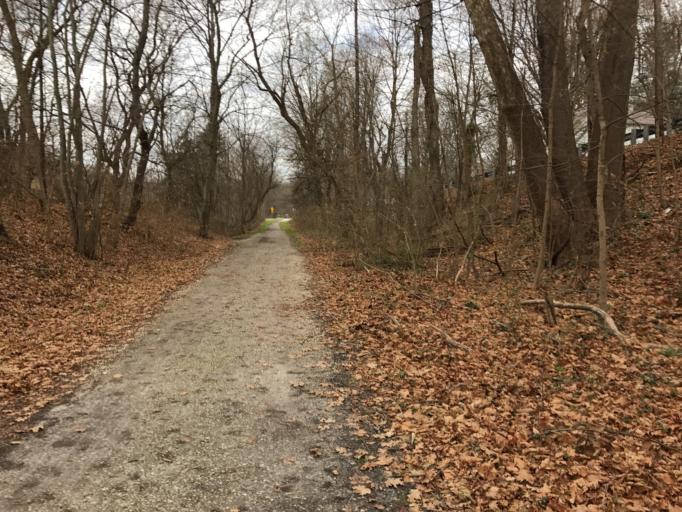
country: US
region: Maryland
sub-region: Baltimore County
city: Hunt Valley
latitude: 39.6206
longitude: -76.6278
